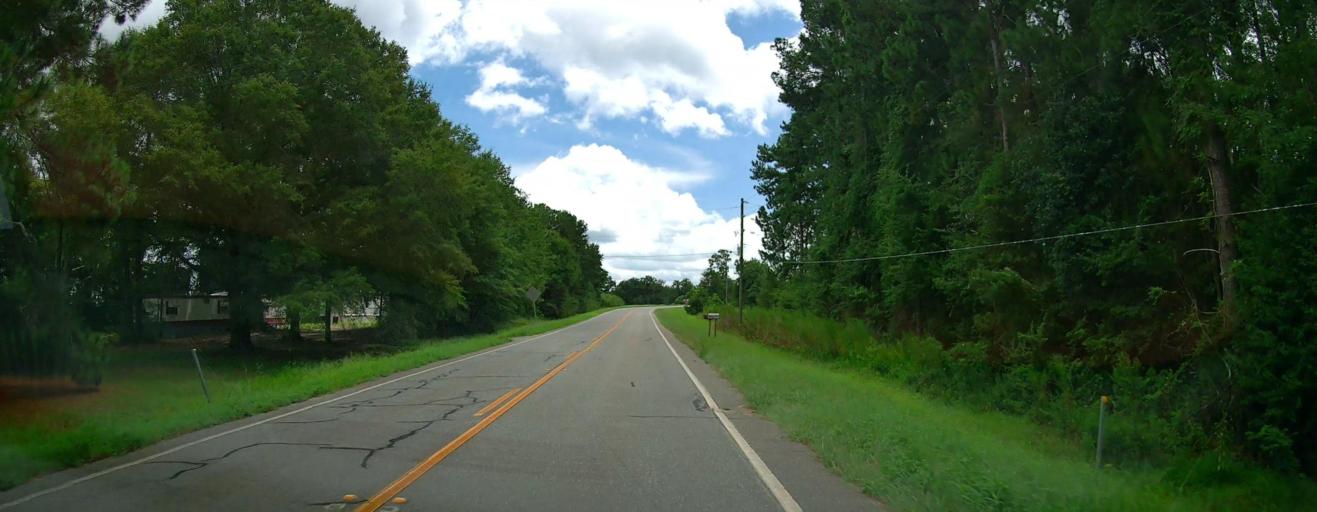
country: US
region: Georgia
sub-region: Wilcox County
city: Rochelle
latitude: 31.9614
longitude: -83.5426
